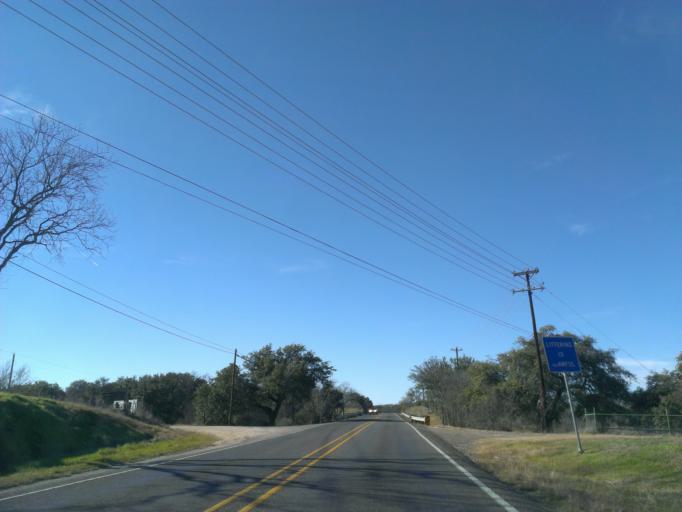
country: US
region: Texas
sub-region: Burnet County
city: Cottonwood Shores
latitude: 30.5463
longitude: -98.3094
